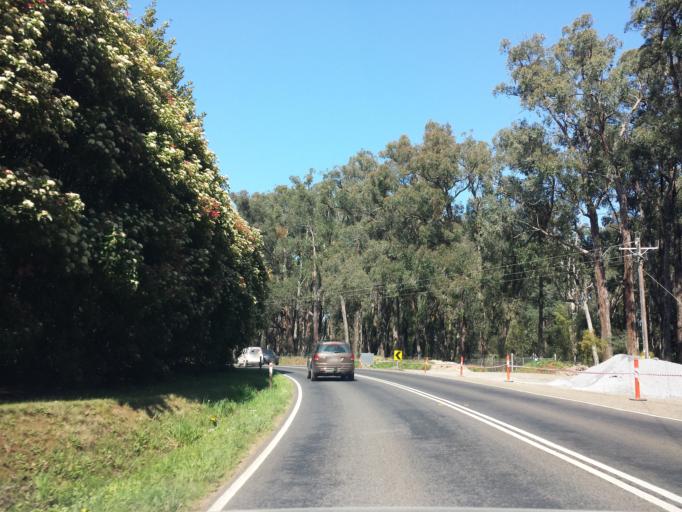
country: AU
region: Victoria
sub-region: Yarra Ranges
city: Monbulk
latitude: -37.8462
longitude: 145.4227
